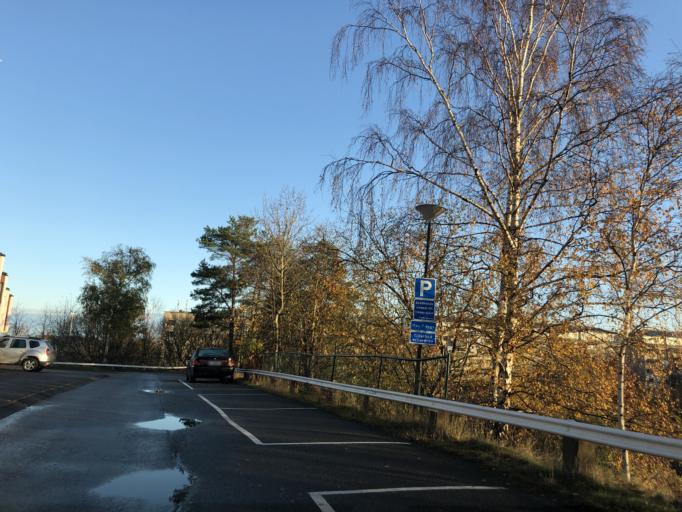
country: SE
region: Vaestra Goetaland
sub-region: Goteborg
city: Hammarkullen
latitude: 57.7797
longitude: 12.0298
